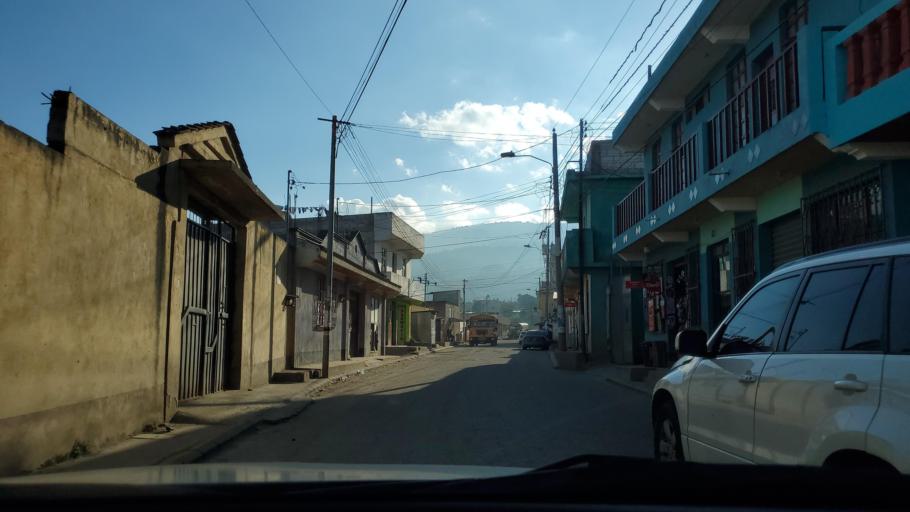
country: GT
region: Quetzaltenango
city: Quetzaltenango
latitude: 14.8381
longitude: -91.5447
